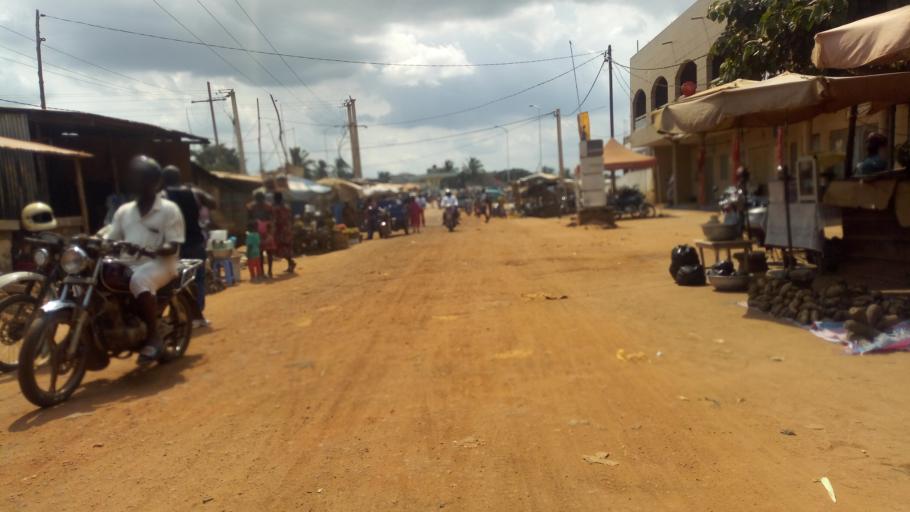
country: TG
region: Maritime
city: Tsevie
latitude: 6.3232
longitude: 1.2192
